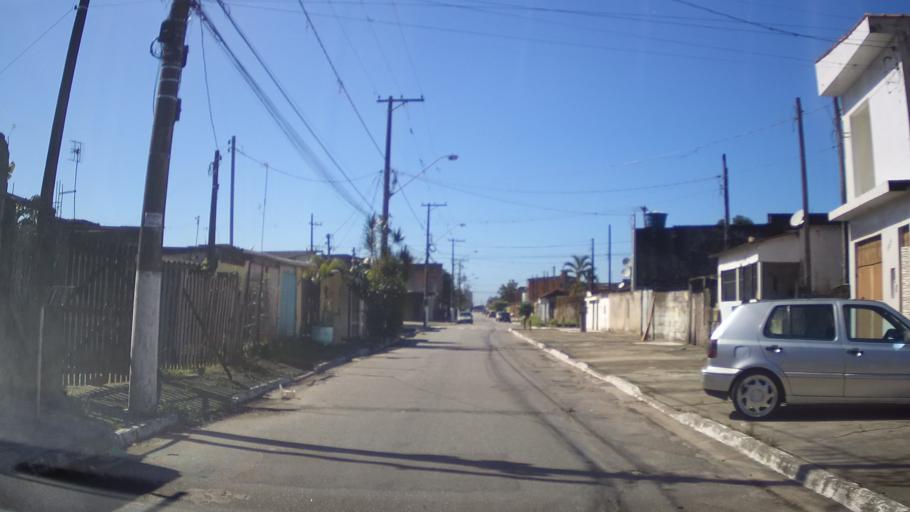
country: BR
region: Sao Paulo
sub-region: Praia Grande
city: Praia Grande
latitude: -24.0318
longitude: -46.5175
